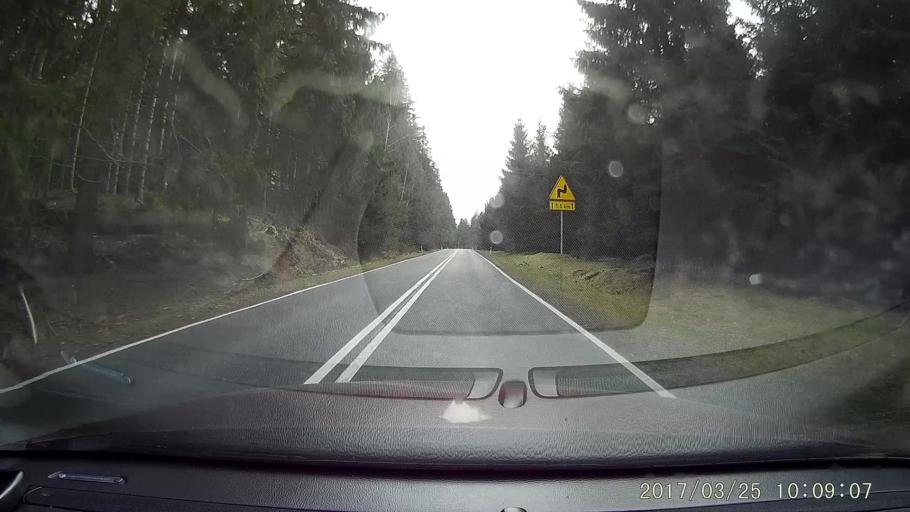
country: PL
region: Lower Silesian Voivodeship
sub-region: Powiat lubanski
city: Swieradow-Zdroj
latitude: 50.8852
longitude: 15.3926
